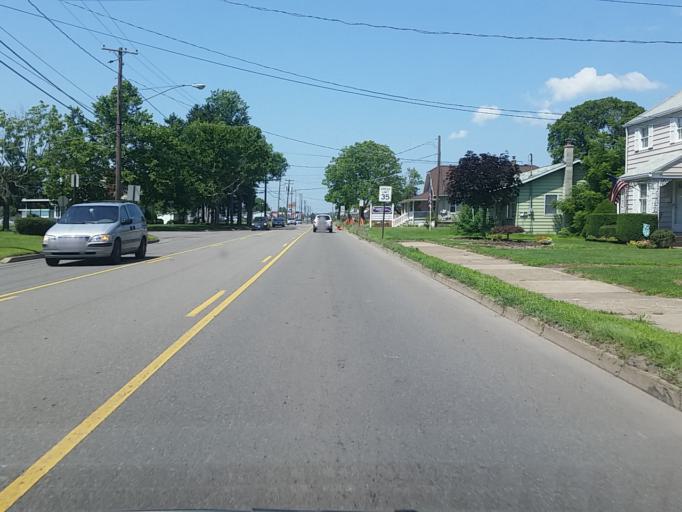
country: US
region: Pennsylvania
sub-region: Columbia County
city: Berwick
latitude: 41.0482
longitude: -76.2644
